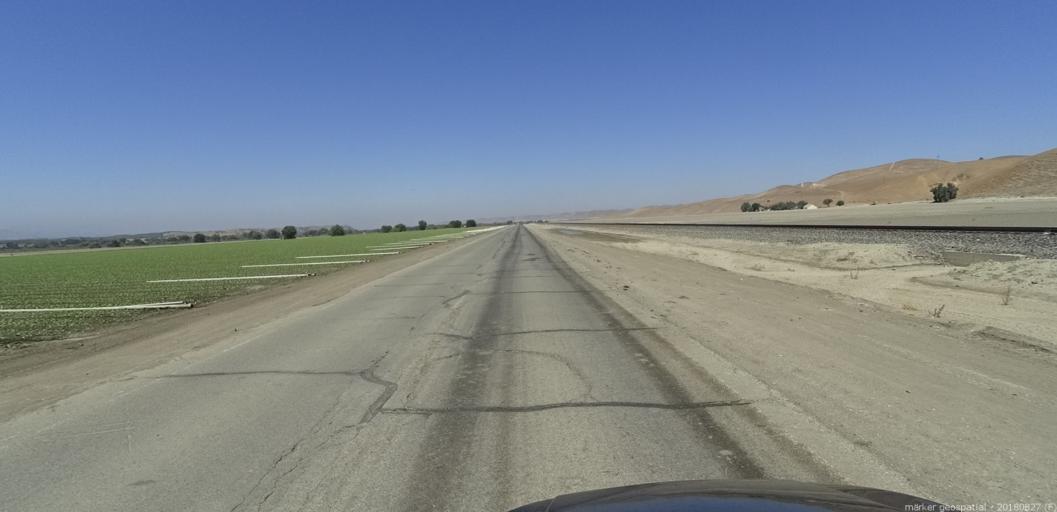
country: US
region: California
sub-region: Monterey County
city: King City
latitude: 36.0395
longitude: -120.9137
